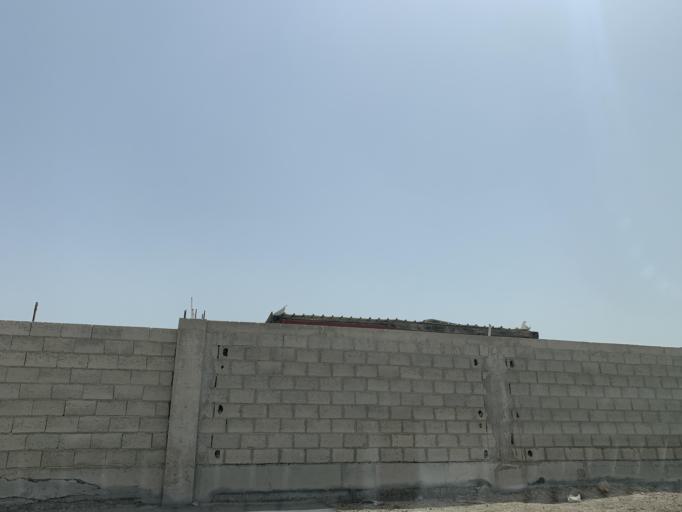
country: BH
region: Northern
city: Madinat `Isa
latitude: 26.1651
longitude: 50.5214
